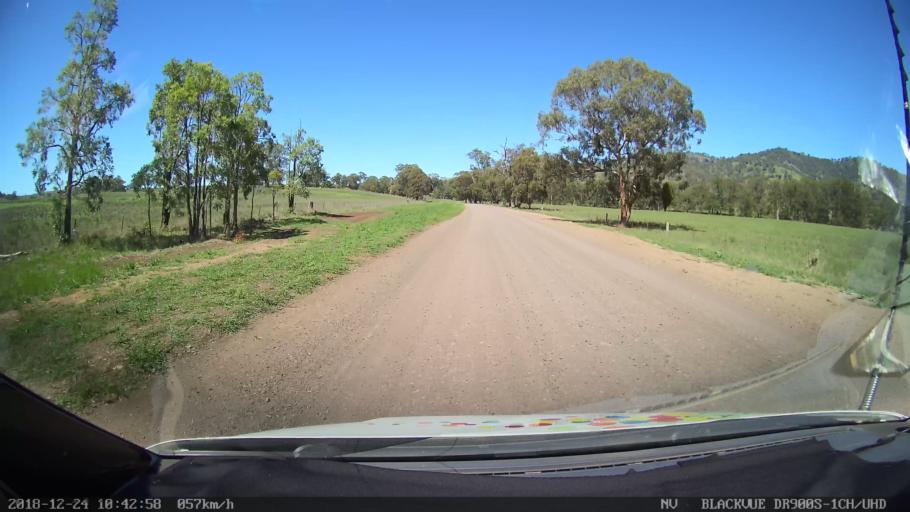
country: AU
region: New South Wales
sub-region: Upper Hunter Shire
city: Merriwa
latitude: -31.8796
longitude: 150.4495
